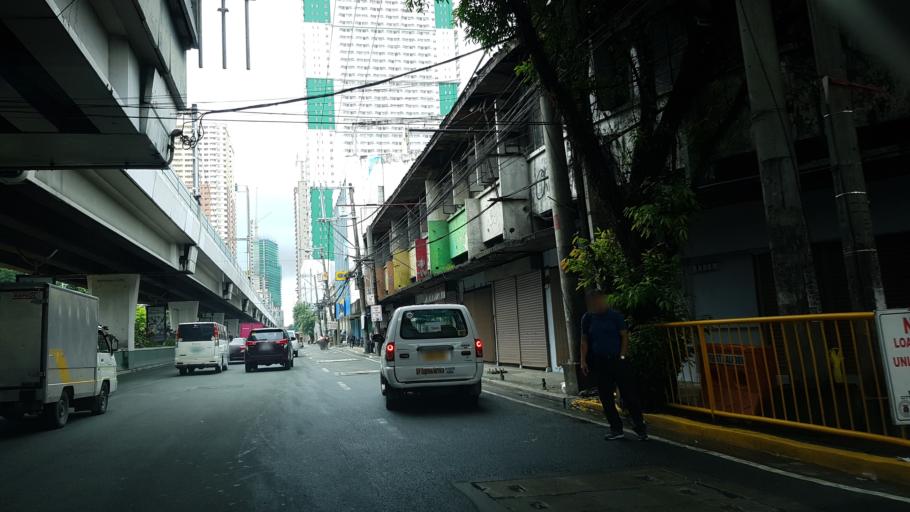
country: PH
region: Metro Manila
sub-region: City of Manila
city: Port Area
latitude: 14.5701
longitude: 120.9916
